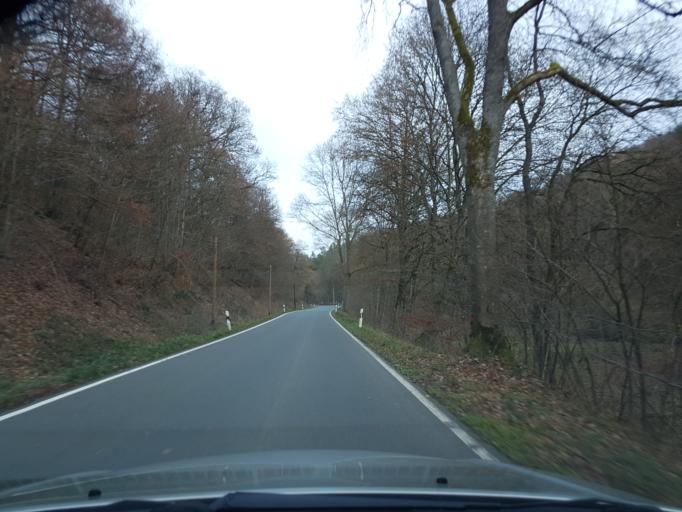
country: DE
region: Hesse
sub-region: Regierungsbezirk Darmstadt
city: Bad Schwalbach
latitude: 50.1340
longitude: 8.0224
